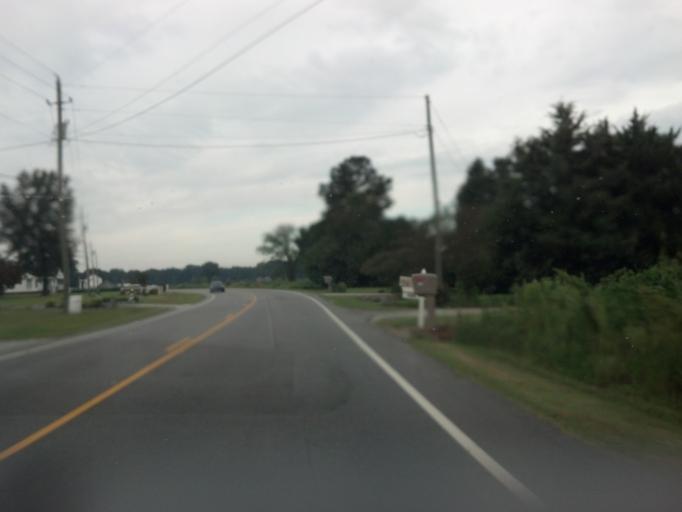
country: US
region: North Carolina
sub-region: Pitt County
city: Ayden
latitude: 35.4769
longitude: -77.4592
